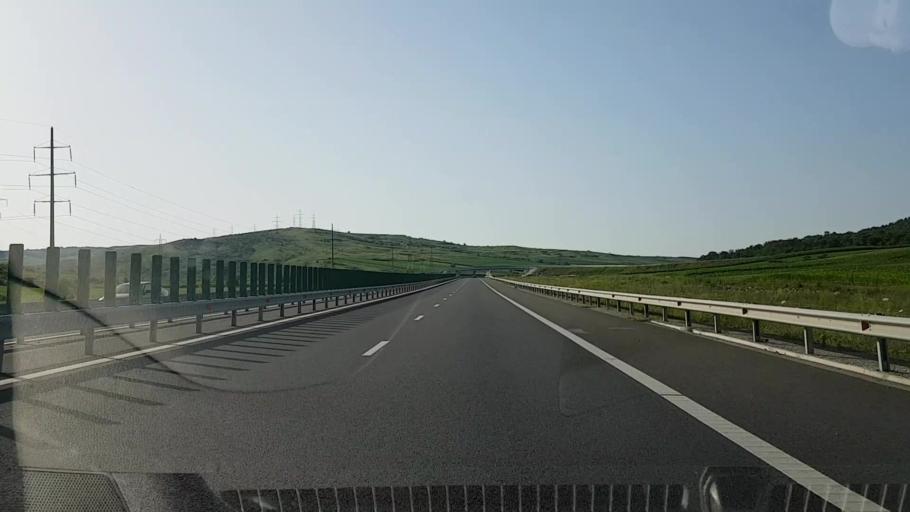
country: RO
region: Alba
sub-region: Comuna Unirea
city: Unirea
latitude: 46.4633
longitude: 23.7812
